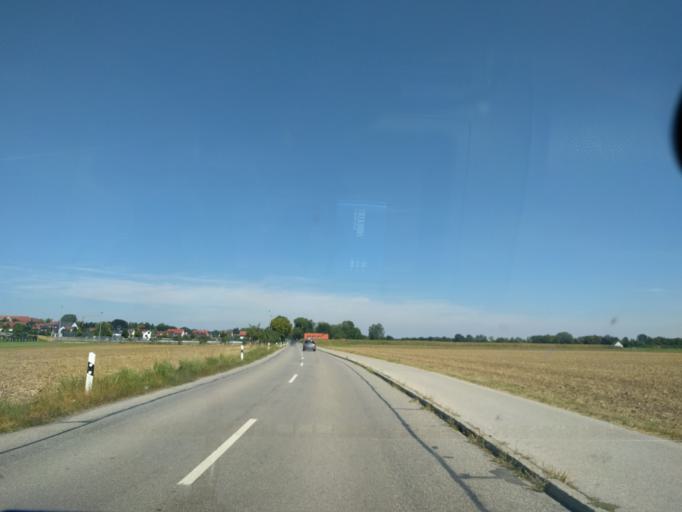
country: DE
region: Bavaria
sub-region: Upper Bavaria
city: Fuerstenfeldbruck
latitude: 48.1827
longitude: 11.2247
